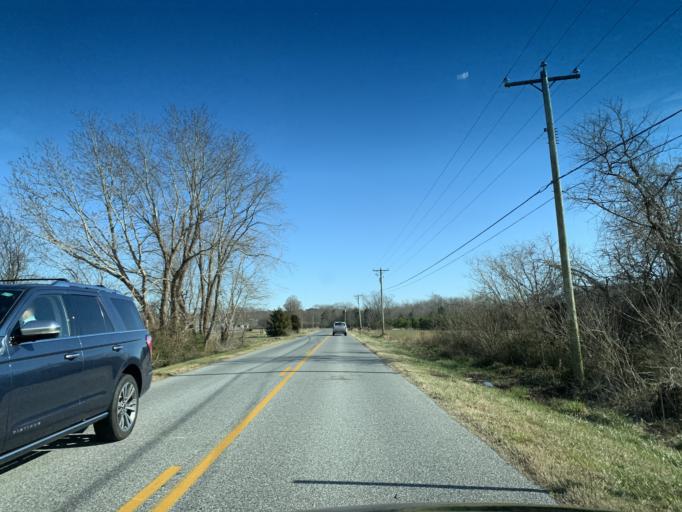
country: US
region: Maryland
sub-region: Worcester County
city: Ocean Pines
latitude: 38.4193
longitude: -75.1473
